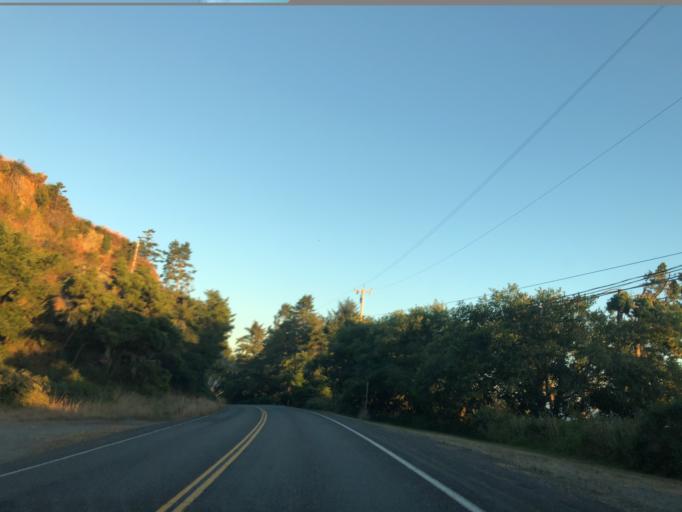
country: US
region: California
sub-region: Humboldt County
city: Westhaven-Moonstone
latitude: 41.0960
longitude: -124.1570
